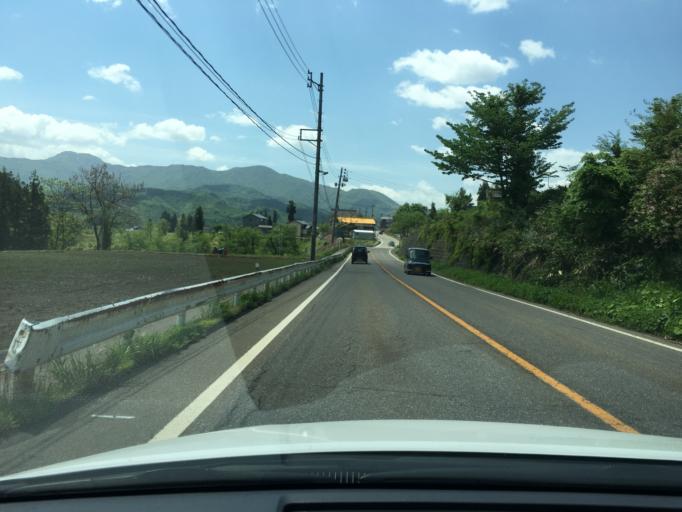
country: JP
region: Niigata
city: Tochio-honcho
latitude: 37.3324
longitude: 139.0275
